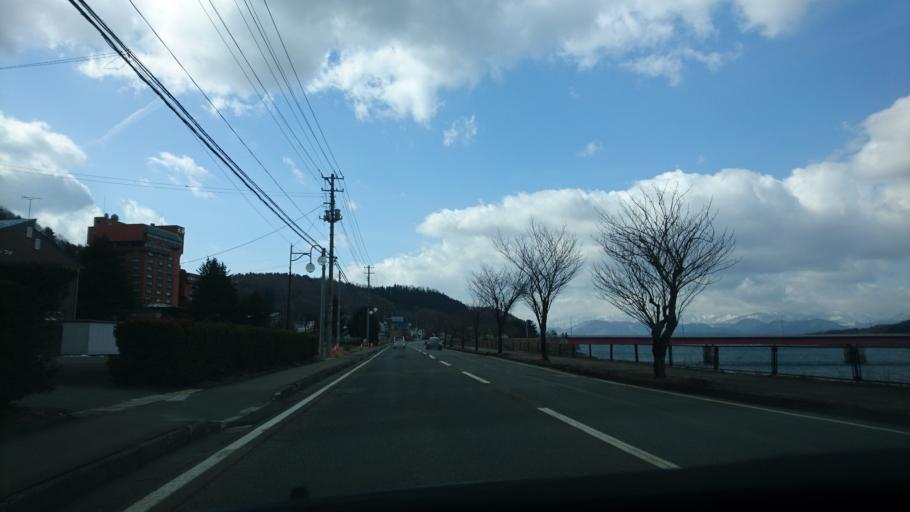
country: JP
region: Iwate
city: Shizukuishi
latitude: 39.6783
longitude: 141.0233
